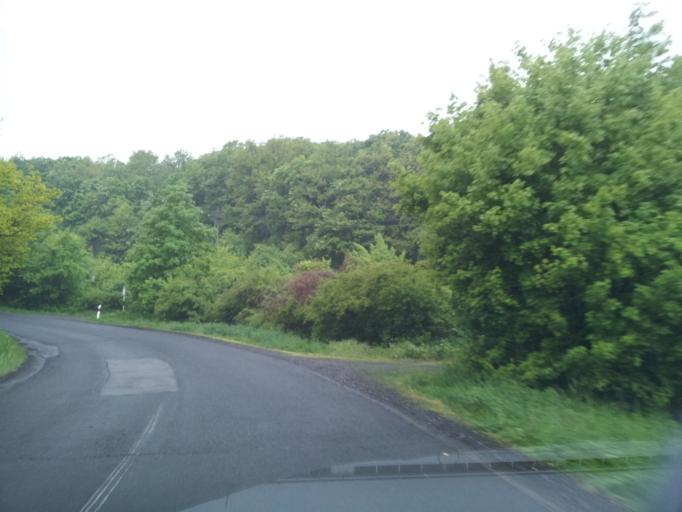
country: HU
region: Baranya
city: Hosszuheteny
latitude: 46.1703
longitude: 18.3406
